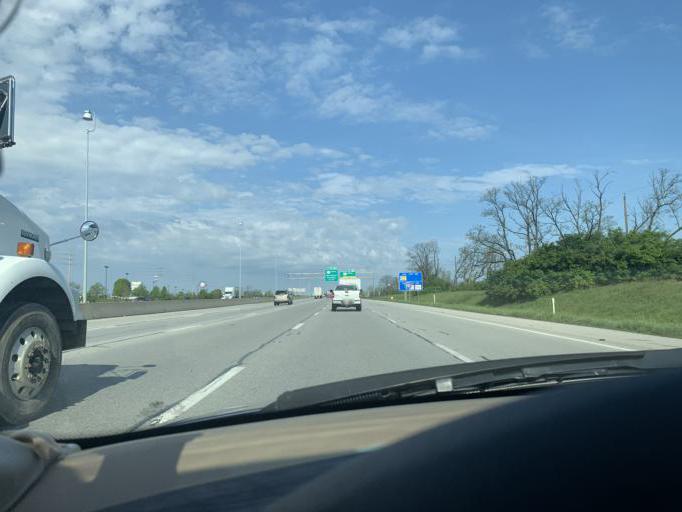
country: US
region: Ohio
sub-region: Hamilton County
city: Glendale
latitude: 39.2933
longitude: -84.4519
